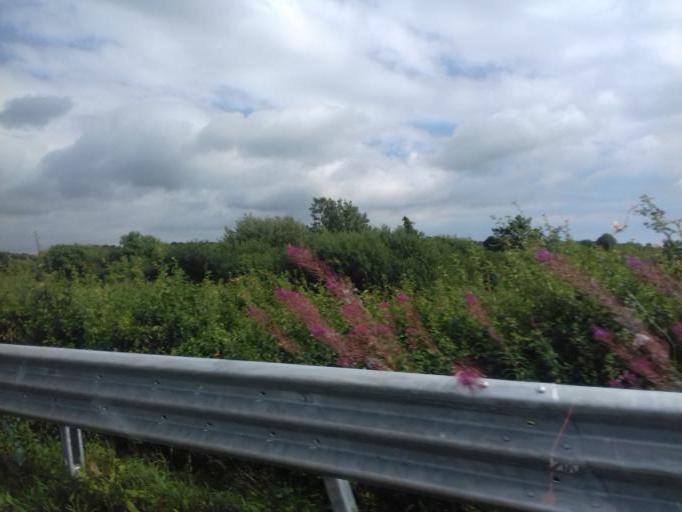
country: IE
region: Leinster
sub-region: Loch Garman
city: Loch Garman
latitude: 52.3283
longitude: -6.6321
